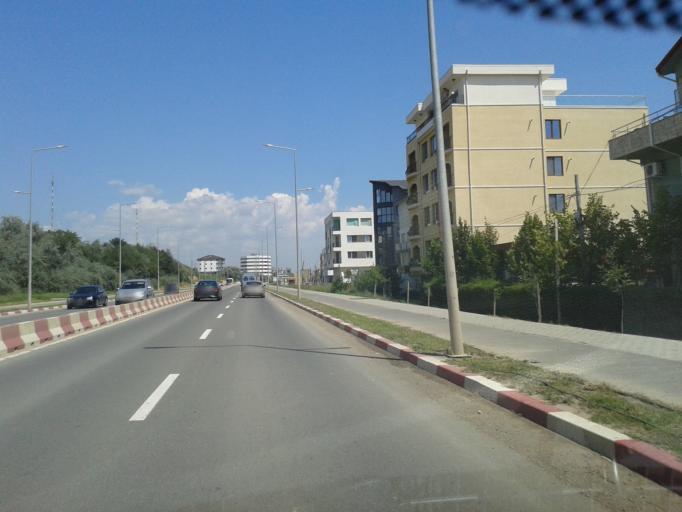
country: RO
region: Constanta
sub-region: Comuna Navodari
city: Navodari
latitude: 44.2971
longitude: 28.6194
